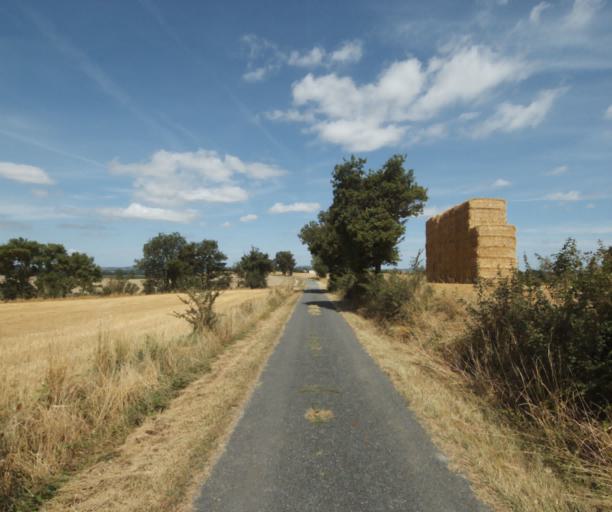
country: FR
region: Midi-Pyrenees
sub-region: Departement du Tarn
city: Dourgne
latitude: 43.4919
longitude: 2.1043
